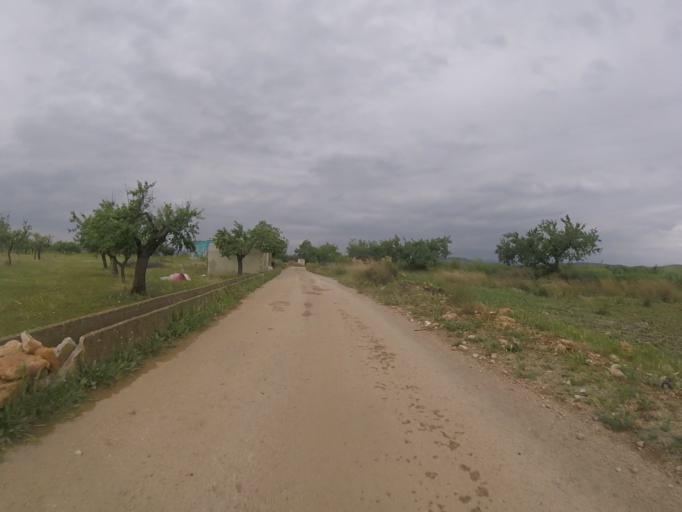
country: ES
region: Valencia
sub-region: Provincia de Castello
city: Torreblanca
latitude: 40.2169
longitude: 0.2288
